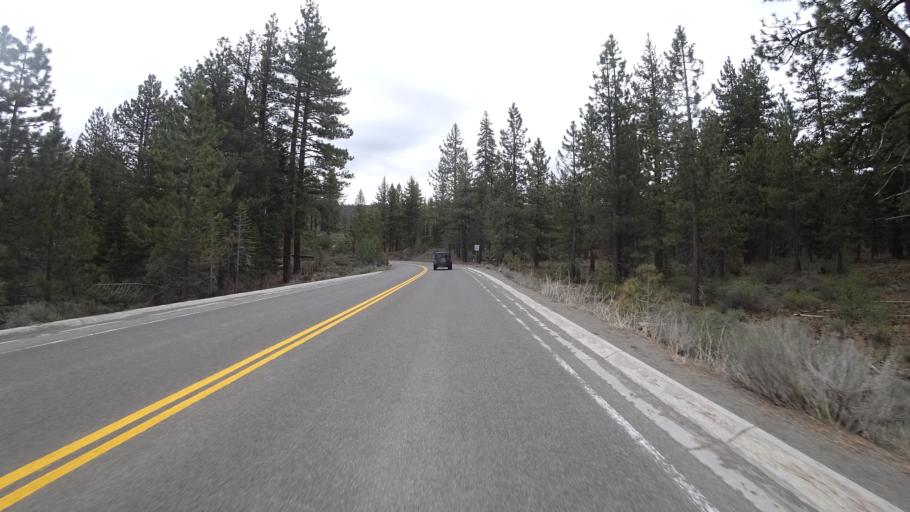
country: US
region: Nevada
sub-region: Douglas County
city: Kingsbury
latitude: 39.1042
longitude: -119.9162
